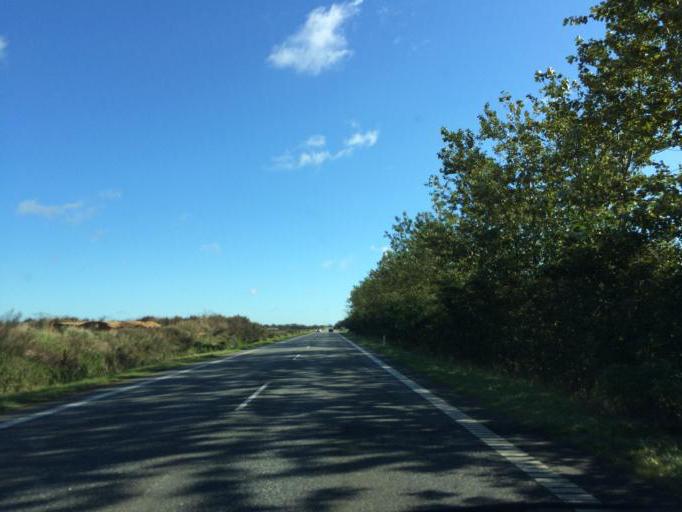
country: DK
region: Central Jutland
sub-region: Holstebro Kommune
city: Vinderup
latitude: 56.3996
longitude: 8.9127
